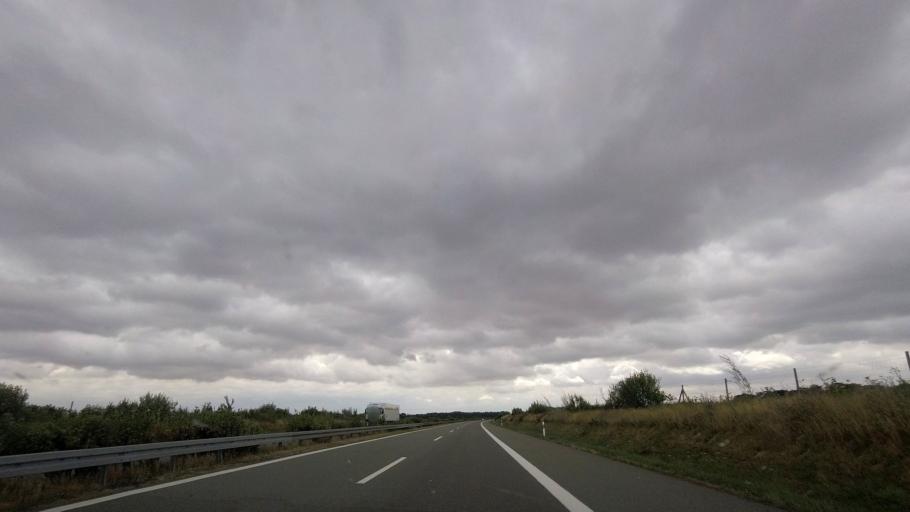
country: DE
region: Mecklenburg-Vorpommern
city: Jarmen
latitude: 53.9747
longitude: 13.3592
